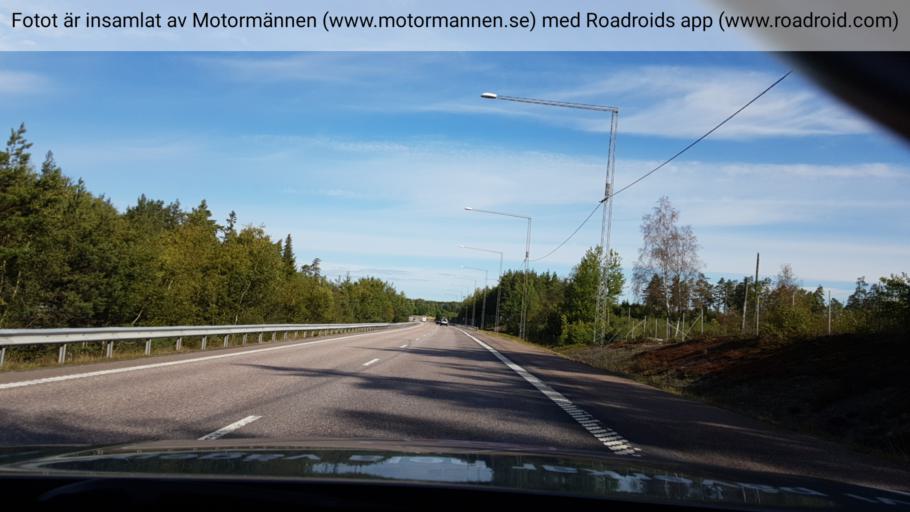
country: SE
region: Stockholm
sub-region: Sigtuna Kommun
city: Marsta
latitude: 59.6272
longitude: 17.9011
